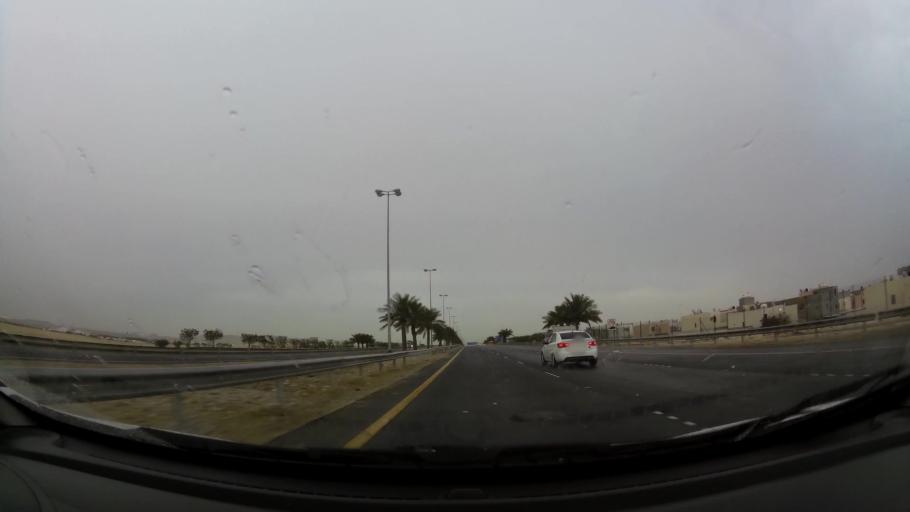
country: BH
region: Central Governorate
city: Dar Kulayb
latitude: 26.0686
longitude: 50.5155
